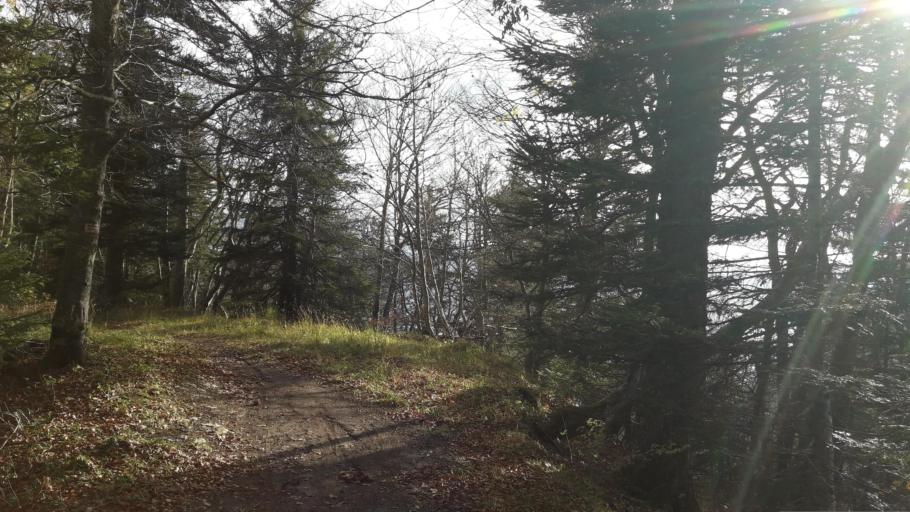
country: FR
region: Rhone-Alpes
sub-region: Departement de l'Isere
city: Bernin
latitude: 45.2953
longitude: 5.8339
